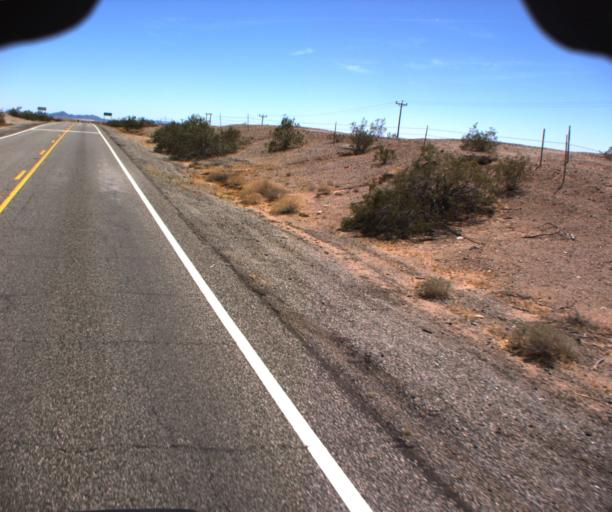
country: US
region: Arizona
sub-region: La Paz County
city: Parker
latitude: 34.0244
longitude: -114.2531
